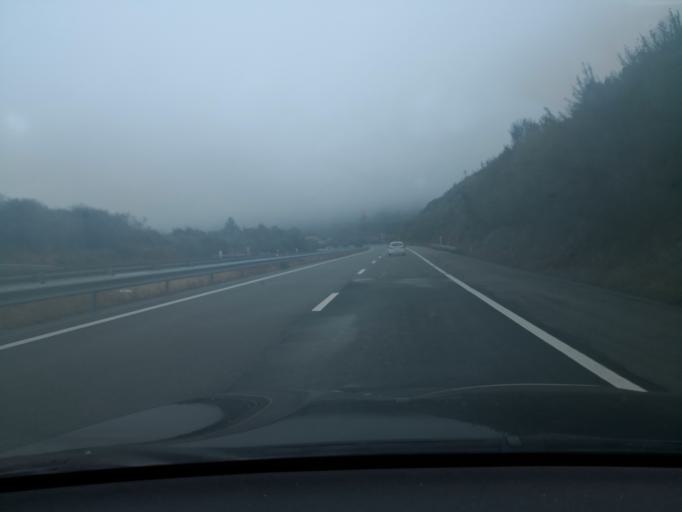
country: PT
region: Braga
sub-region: Celorico de Basto
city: Celorico de Basto
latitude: 41.4476
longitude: -8.0627
